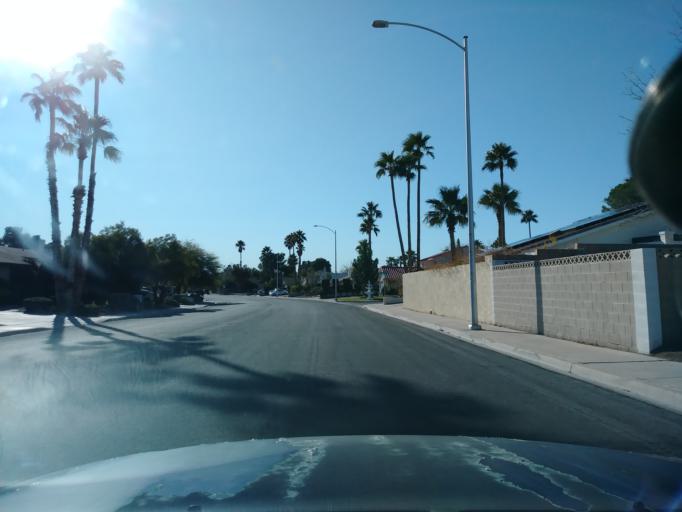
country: US
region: Nevada
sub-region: Clark County
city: Spring Valley
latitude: 36.1506
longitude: -115.2305
